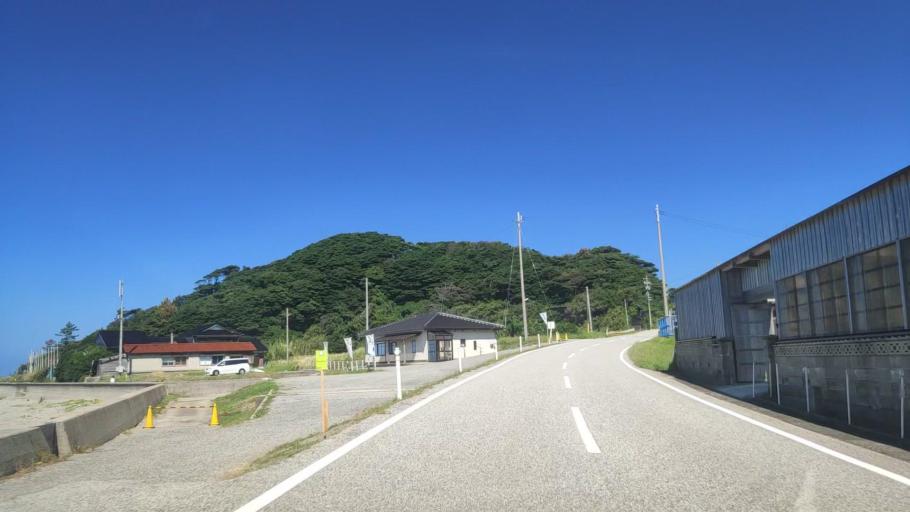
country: JP
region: Ishikawa
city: Nanao
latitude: 37.5121
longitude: 137.2197
